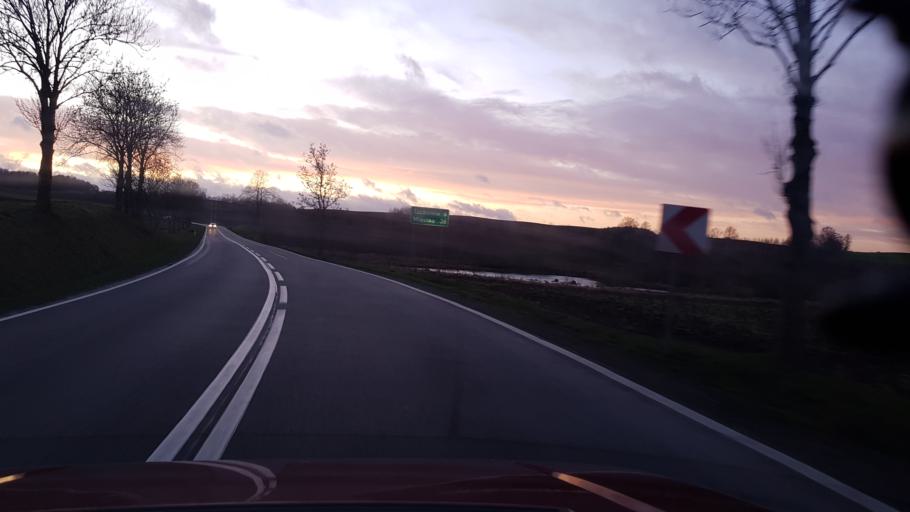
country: PL
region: Pomeranian Voivodeship
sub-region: Powiat bytowski
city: Borzytuchom
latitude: 54.1366
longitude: 17.4143
